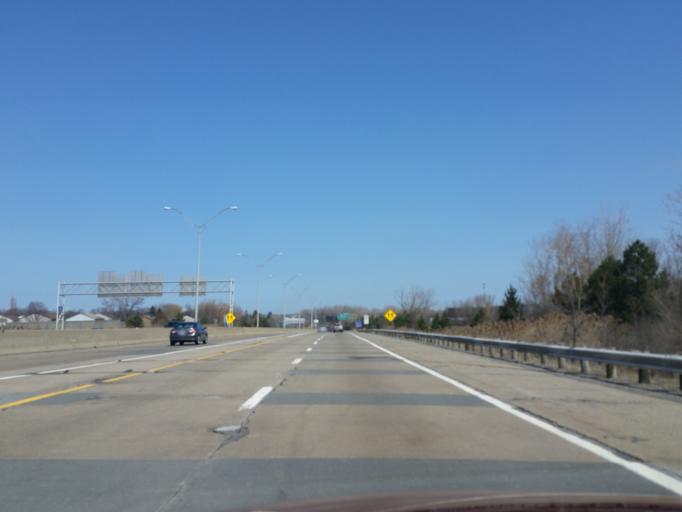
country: US
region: Ohio
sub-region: Cuyahoga County
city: Brooklyn Heights
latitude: 41.4247
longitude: -81.6836
